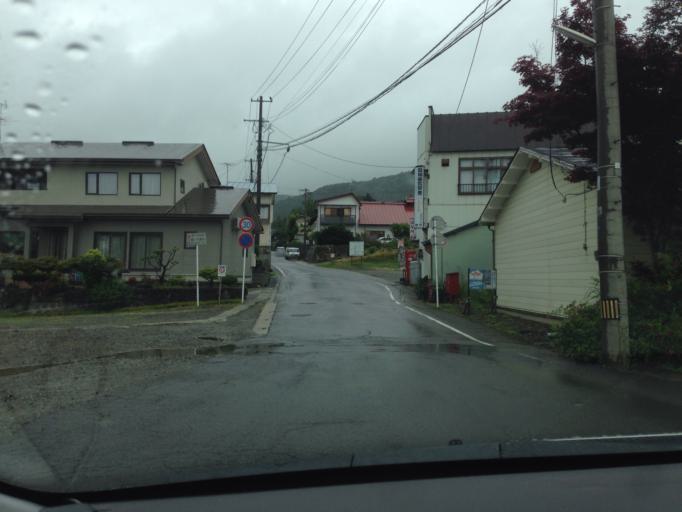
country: JP
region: Fukushima
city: Inawashiro
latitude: 37.5646
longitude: 139.9885
